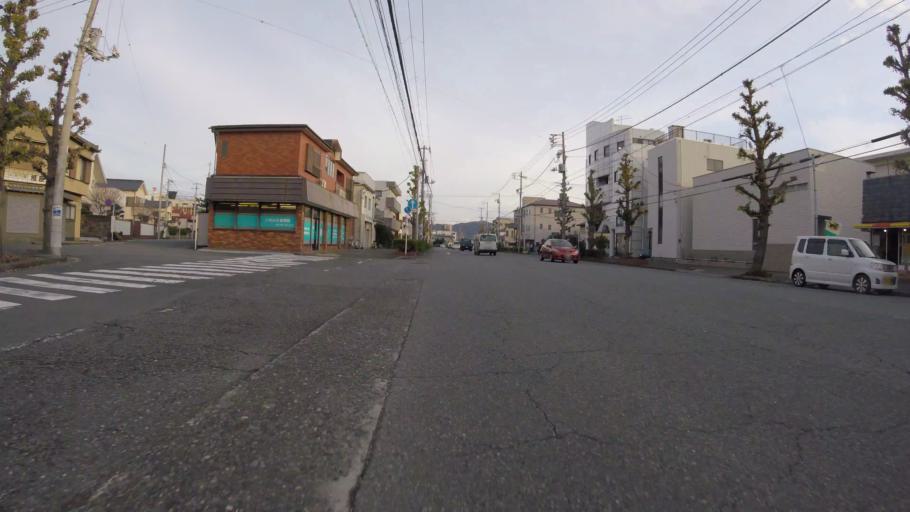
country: JP
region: Shizuoka
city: Numazu
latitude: 35.0989
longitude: 138.8484
